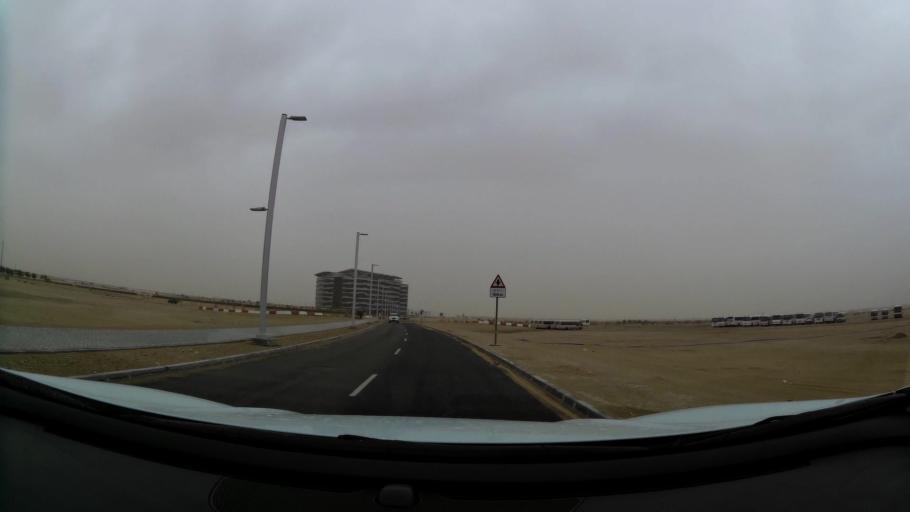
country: AE
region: Abu Dhabi
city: Abu Dhabi
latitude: 24.4304
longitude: 54.6163
